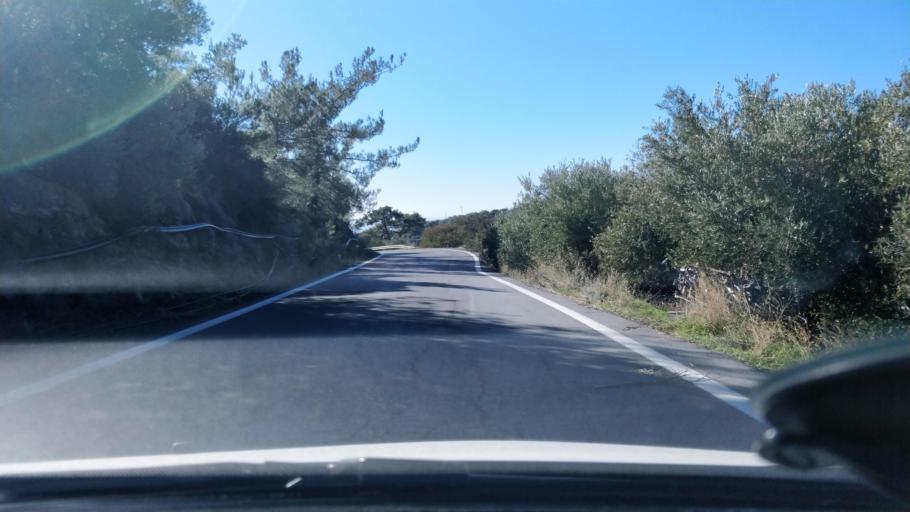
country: GR
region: Crete
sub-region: Nomos Irakleiou
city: Kastelli
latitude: 35.0162
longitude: 25.4482
